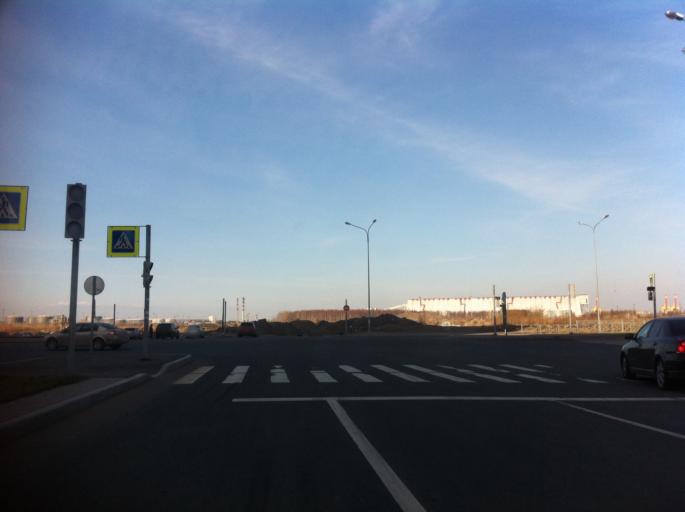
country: RU
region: St.-Petersburg
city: Uritsk
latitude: 59.8683
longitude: 30.1683
